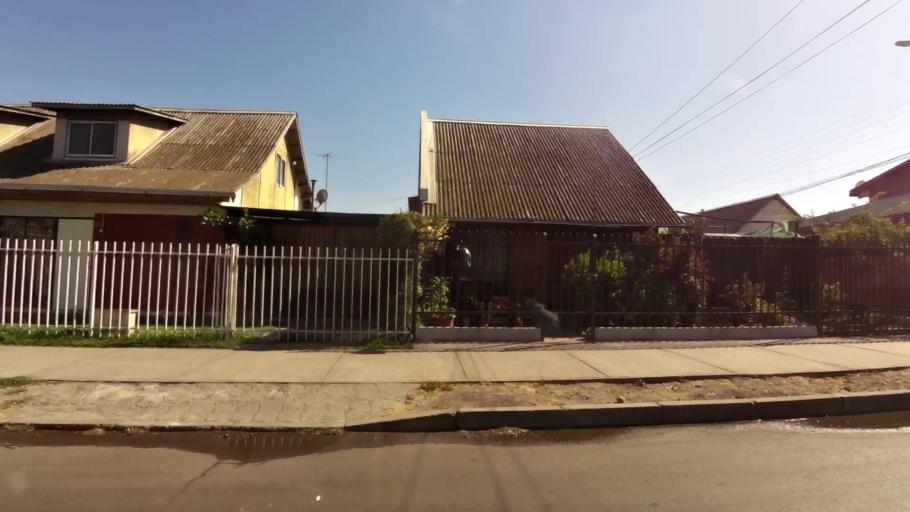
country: CL
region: Maule
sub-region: Provincia de Curico
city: Curico
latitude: -34.9798
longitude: -71.2597
